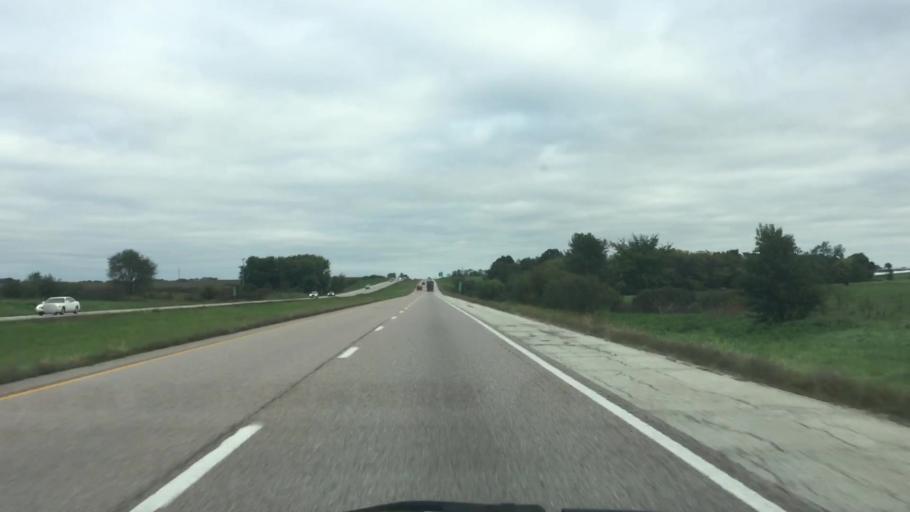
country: US
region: Missouri
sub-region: Clinton County
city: Lathrop
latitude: 39.5255
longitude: -94.2802
